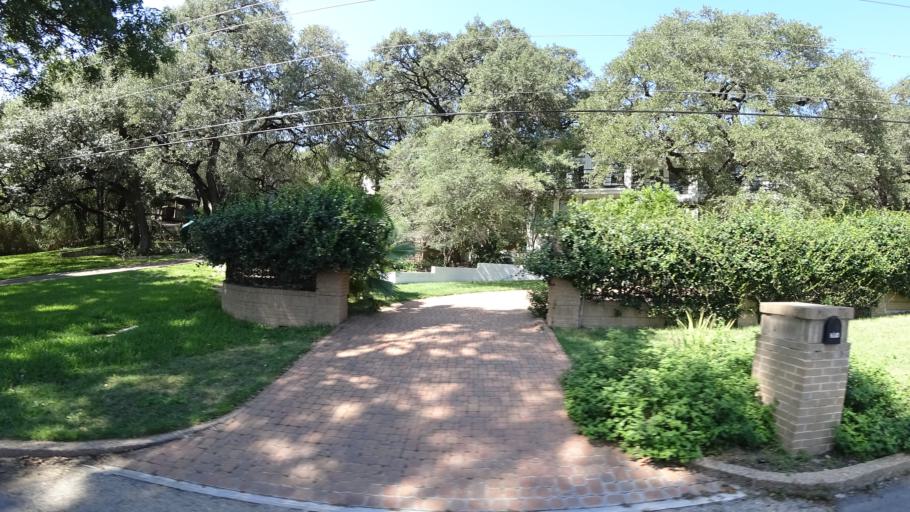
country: US
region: Texas
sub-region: Travis County
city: West Lake Hills
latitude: 30.3075
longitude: -97.7817
